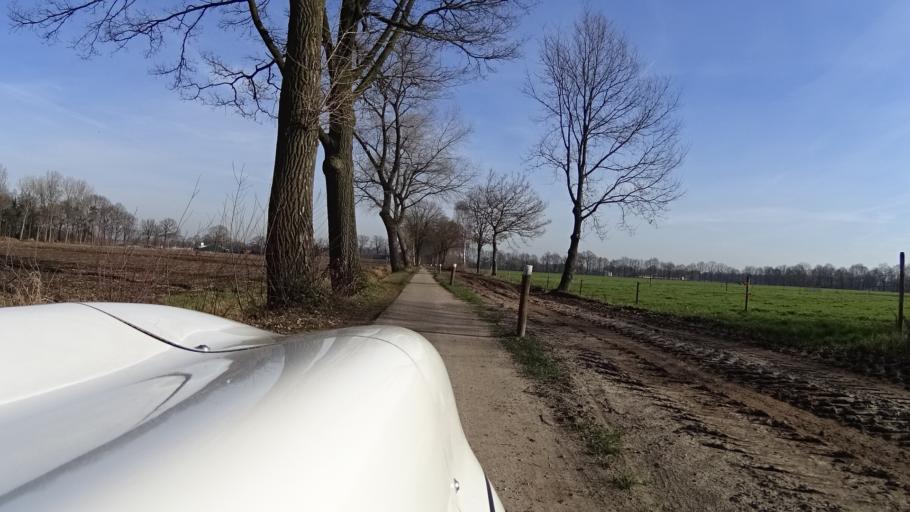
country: NL
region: North Brabant
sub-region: Gemeente Veghel
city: Mariaheide
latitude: 51.6118
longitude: 5.5850
